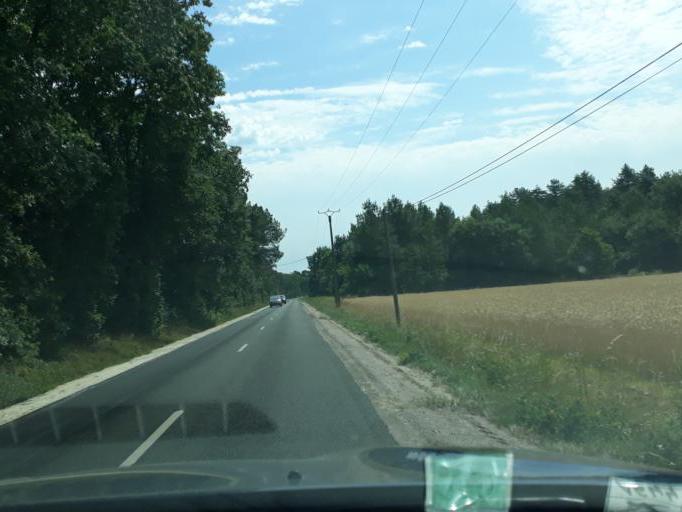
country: FR
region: Centre
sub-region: Departement du Loir-et-Cher
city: Vouzon
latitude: 47.6484
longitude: 2.0211
